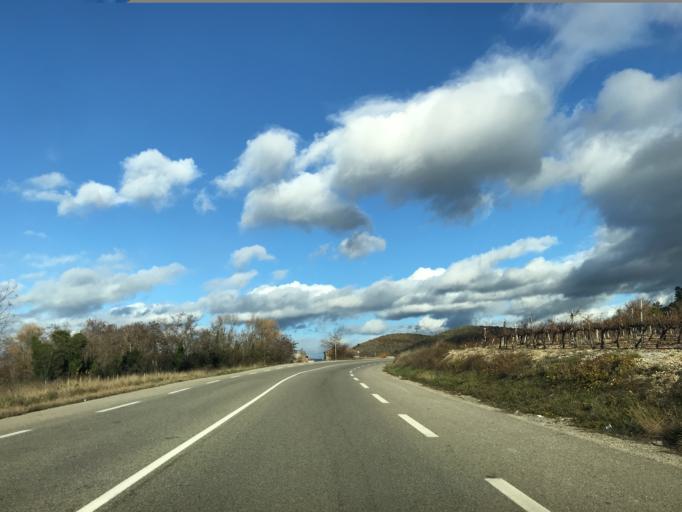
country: FR
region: Rhone-Alpes
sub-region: Departement de l'Ardeche
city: Lachapelle-sous-Aubenas
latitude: 44.5384
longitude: 4.3472
